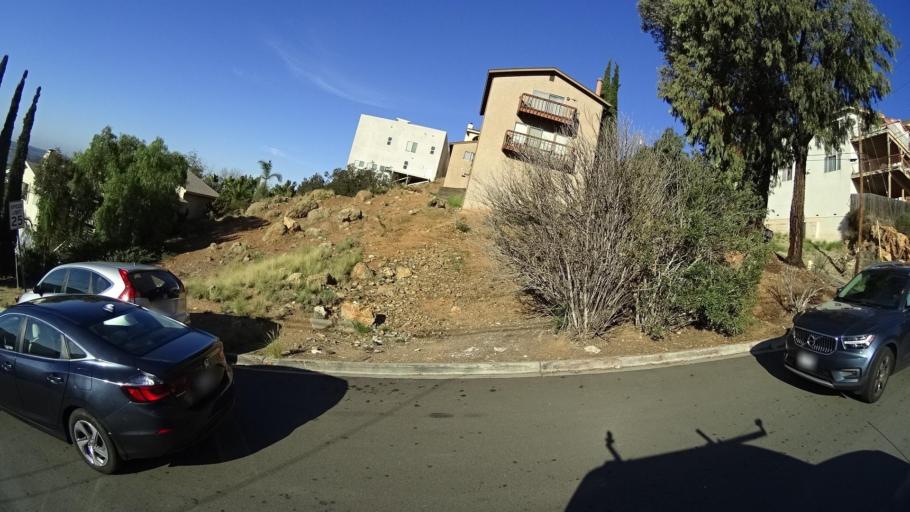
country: US
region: California
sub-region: San Diego County
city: La Presa
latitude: 32.7199
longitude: -116.9863
